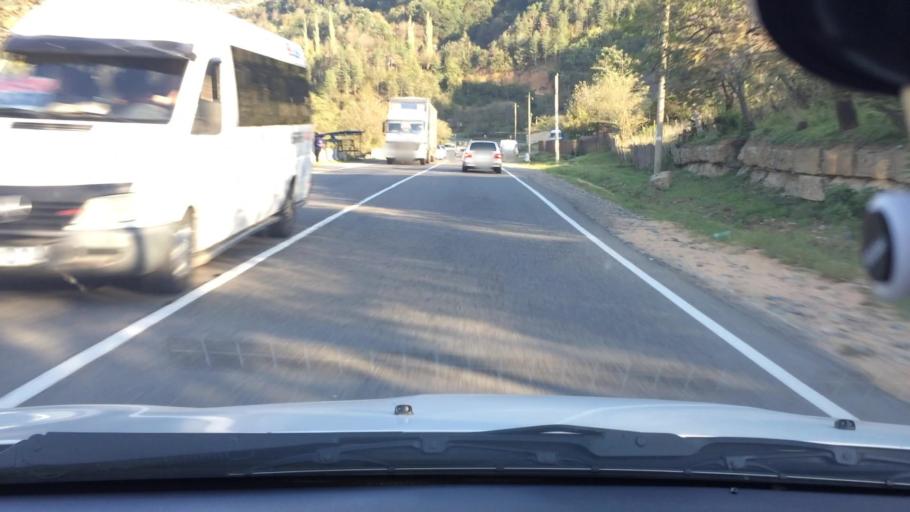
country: GE
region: Imereti
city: Kharagauli
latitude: 42.1055
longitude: 43.3096
